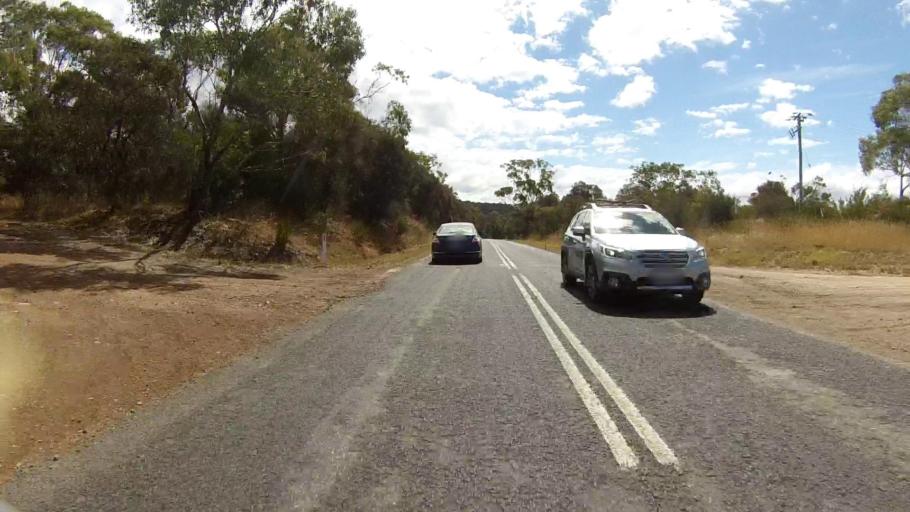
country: AU
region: Tasmania
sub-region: Sorell
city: Sorell
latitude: -42.1557
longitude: 148.0696
